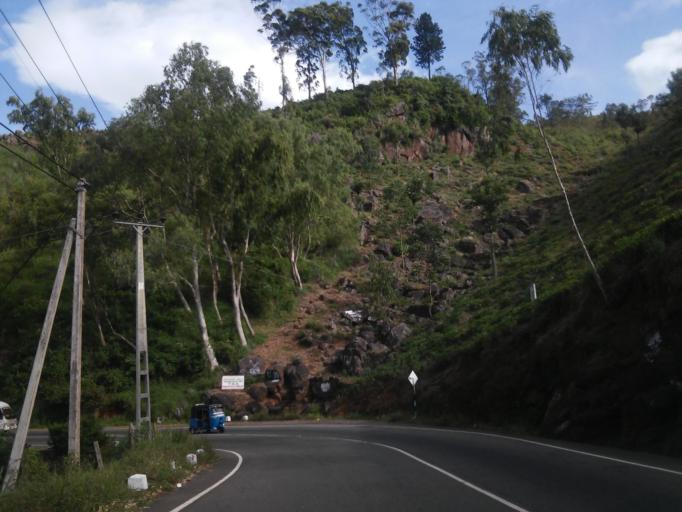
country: LK
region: Uva
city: Haputale
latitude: 6.7597
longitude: 80.9478
